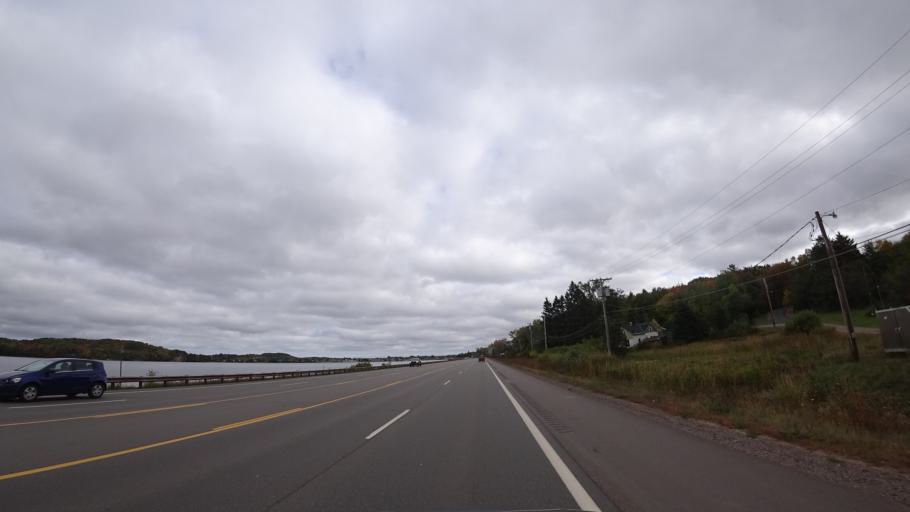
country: US
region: Michigan
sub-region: Marquette County
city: Negaunee
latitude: 46.5107
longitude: -87.6342
